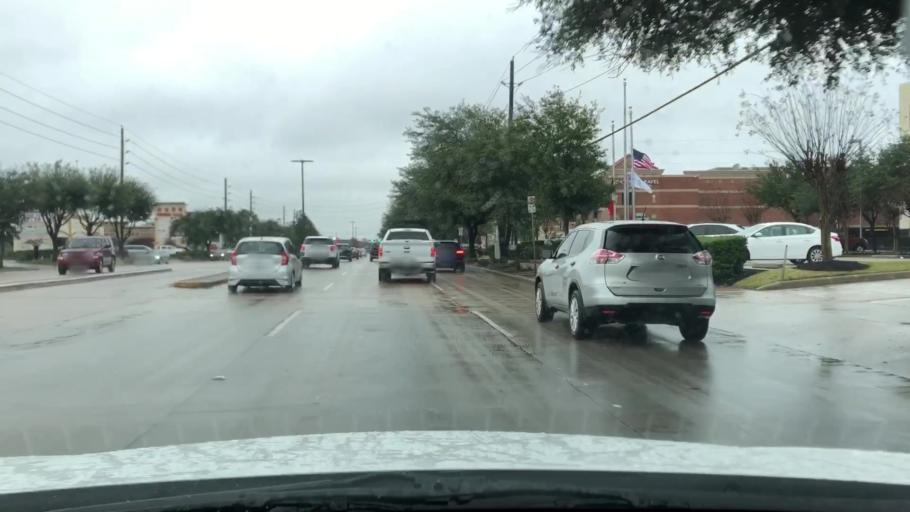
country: US
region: Texas
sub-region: Fort Bend County
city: Meadows Place
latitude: 29.7045
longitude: -95.5558
